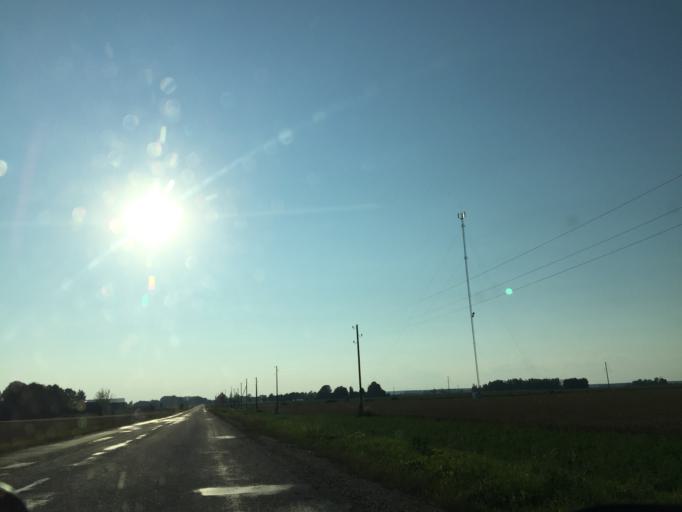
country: LV
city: Tervete
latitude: 56.4377
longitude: 23.5066
